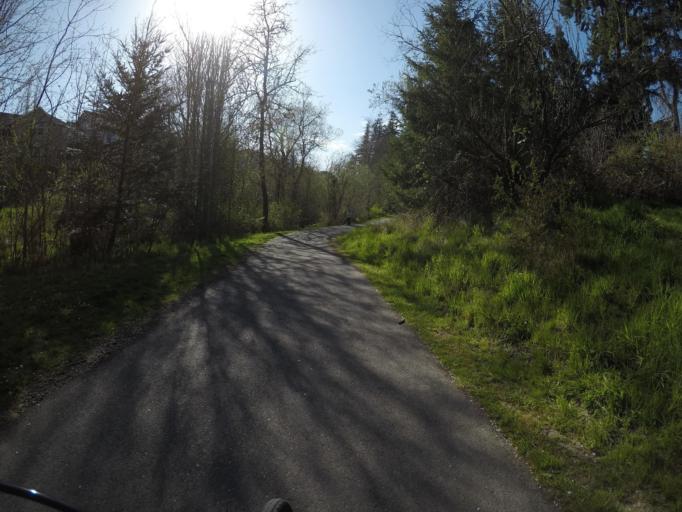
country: US
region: Oregon
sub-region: Washington County
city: Oak Hills
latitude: 45.5556
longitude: -122.8484
